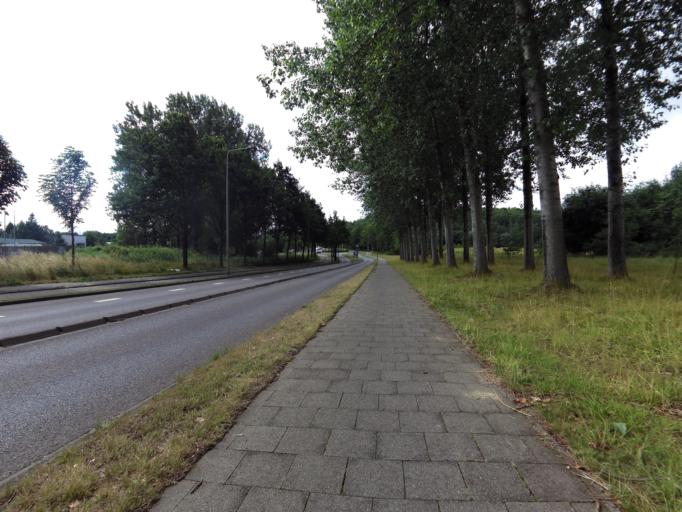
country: NL
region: Limburg
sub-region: Gemeente Heerlen
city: Nieuw-Lotbroek
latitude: 50.9201
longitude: 5.9454
